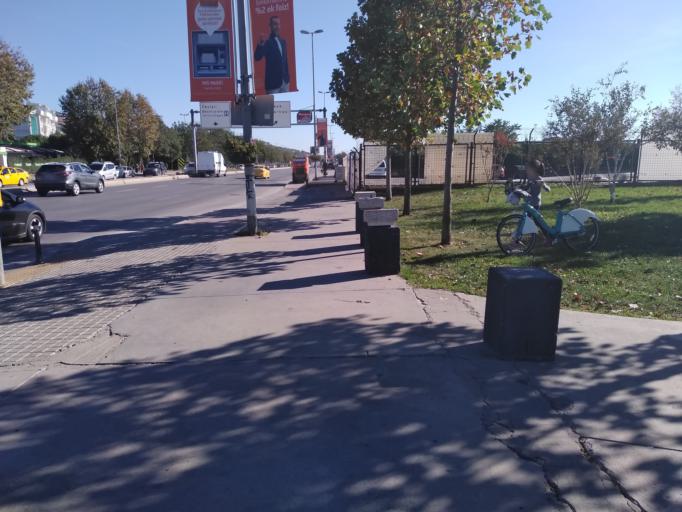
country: TR
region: Istanbul
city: Maltepe
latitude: 40.9198
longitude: 29.1283
